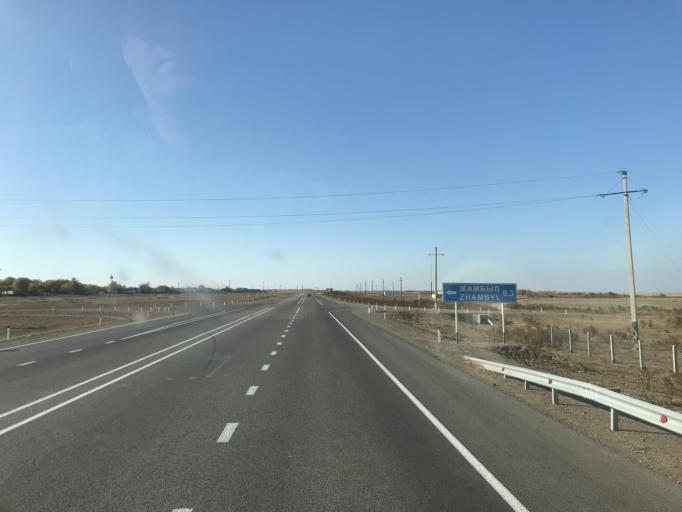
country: KZ
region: Pavlodar
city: Koktobe
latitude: 51.5038
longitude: 77.6992
